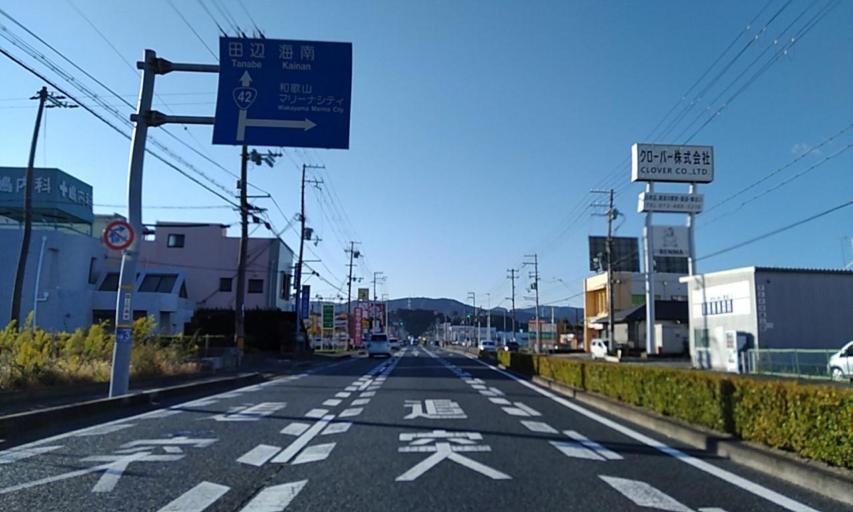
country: JP
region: Wakayama
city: Kainan
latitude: 34.1740
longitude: 135.1867
